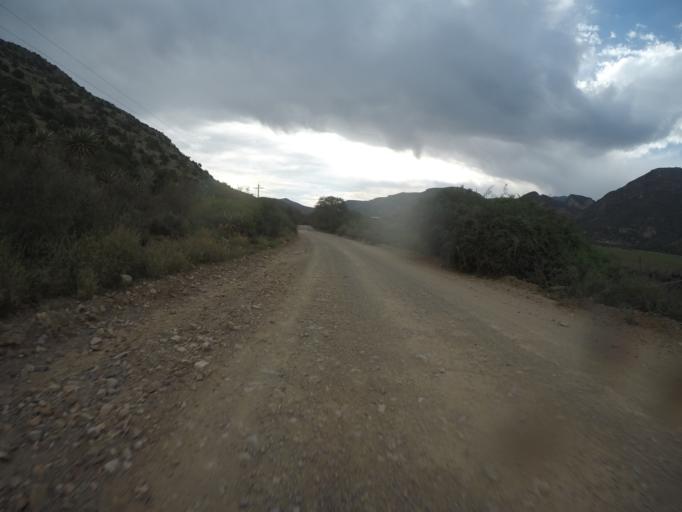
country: ZA
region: Eastern Cape
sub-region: Cacadu District Municipality
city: Willowmore
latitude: -33.5256
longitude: 23.8504
